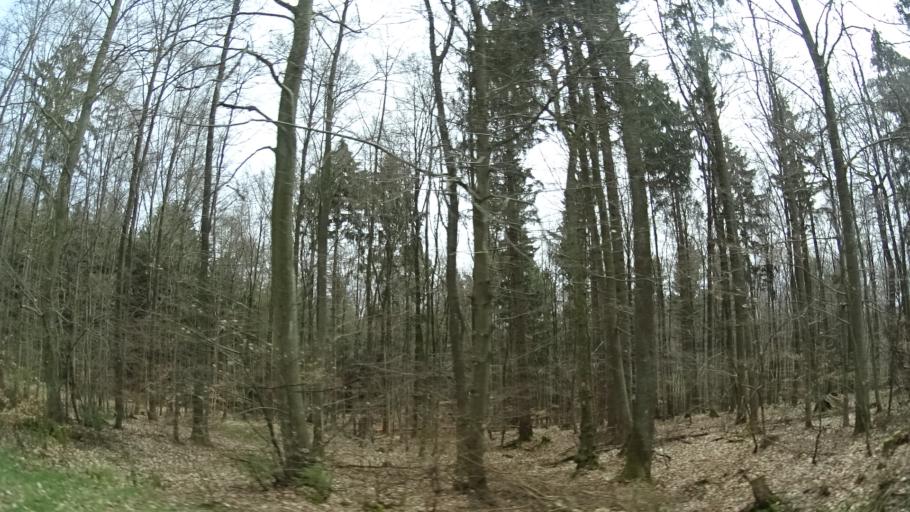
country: DE
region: Rheinland-Pfalz
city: Stipshausen
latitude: 49.8542
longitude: 7.2956
